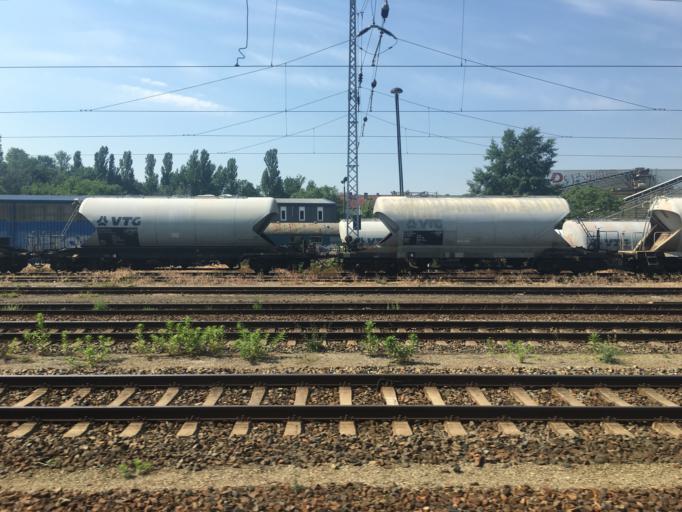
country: DE
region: Berlin
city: Prenzlauer Berg Bezirk
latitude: 52.5387
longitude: 13.4424
